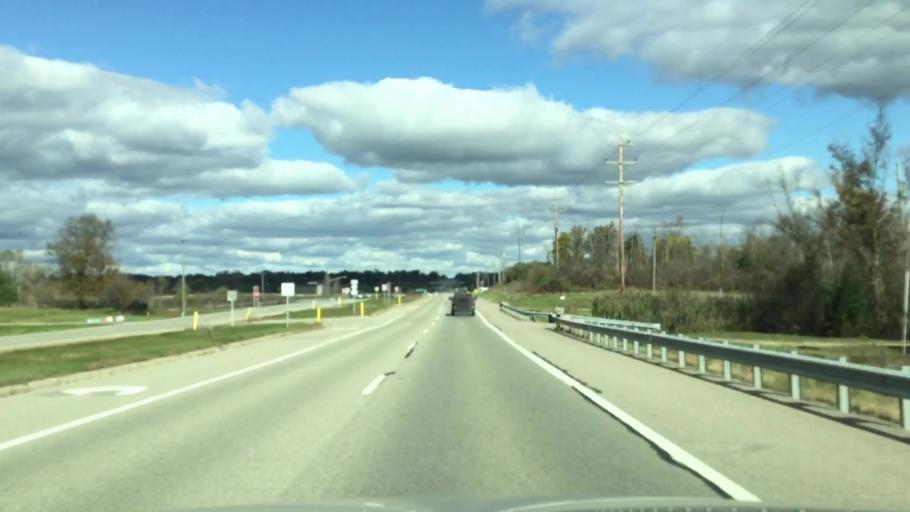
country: US
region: Michigan
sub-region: Lapeer County
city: Lapeer
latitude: 43.0109
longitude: -83.3216
